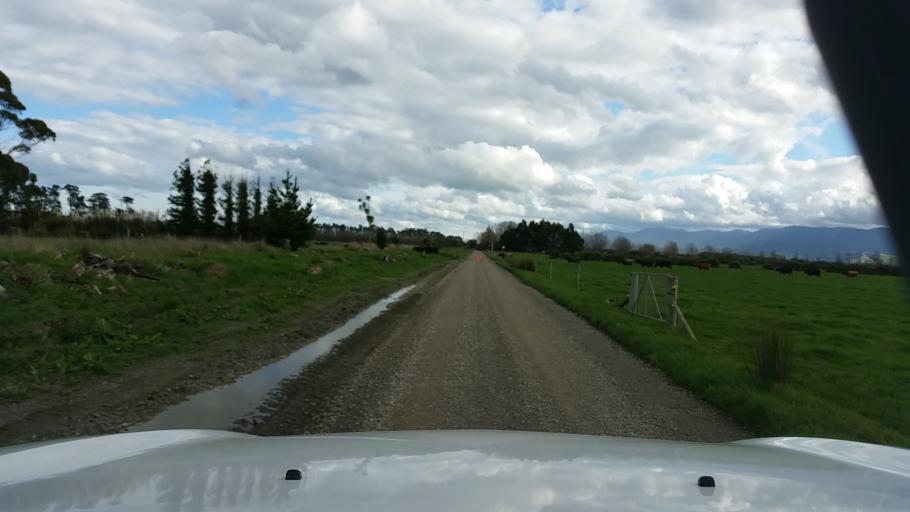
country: NZ
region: Wellington
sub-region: Upper Hutt City
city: Upper Hutt
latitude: -41.2993
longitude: 175.2650
